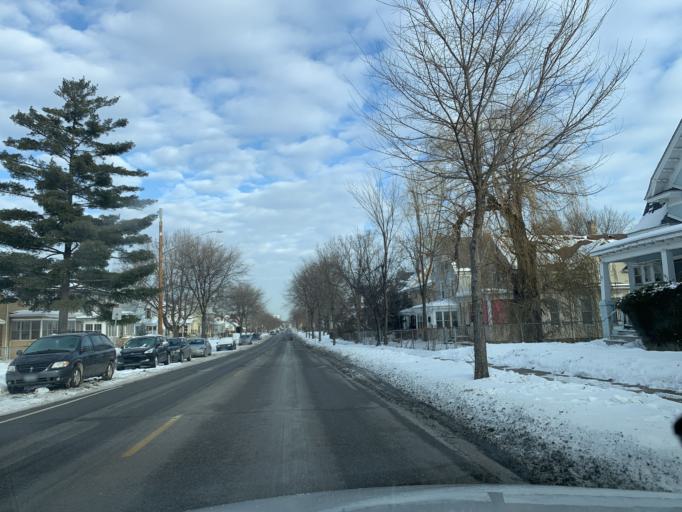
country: US
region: Minnesota
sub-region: Anoka County
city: Columbia Heights
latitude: 45.0242
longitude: -93.2881
